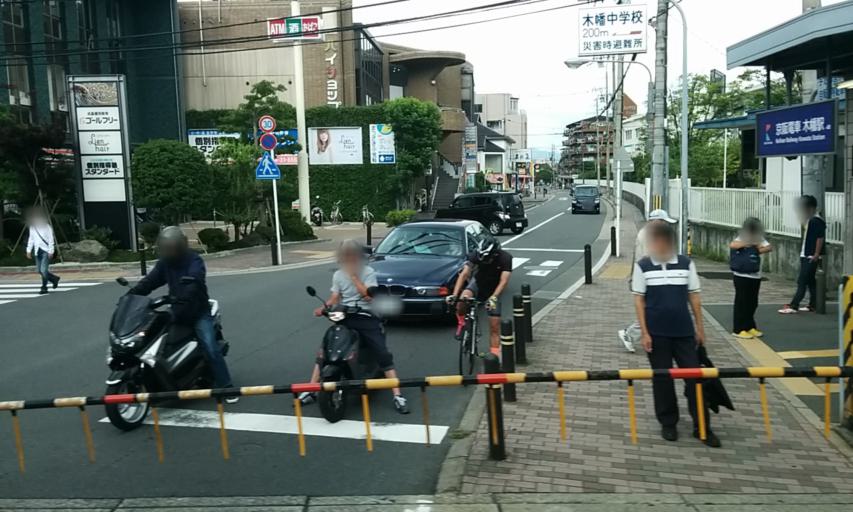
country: JP
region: Kyoto
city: Uji
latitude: 34.9256
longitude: 135.7960
